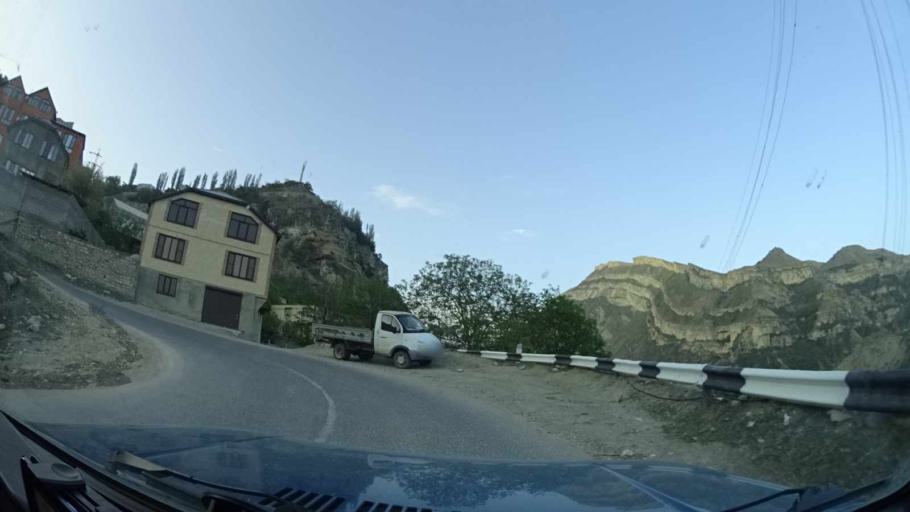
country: RU
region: Dagestan
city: Gunib
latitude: 42.3828
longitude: 46.9633
